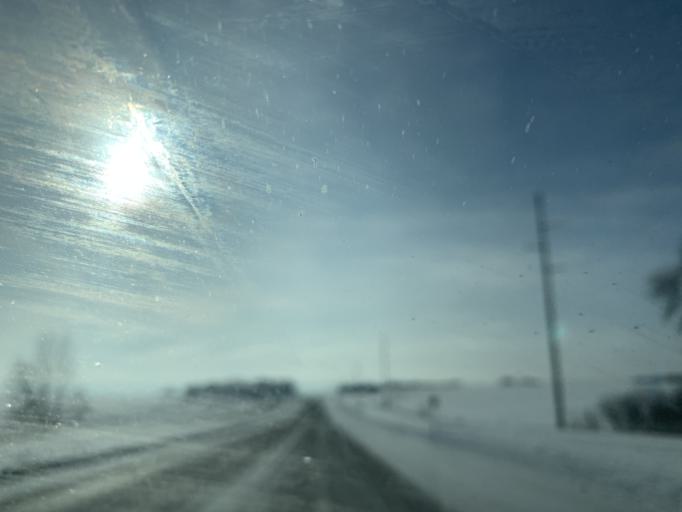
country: US
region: Minnesota
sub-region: Dakota County
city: Lakeville
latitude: 44.6690
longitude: -93.2176
